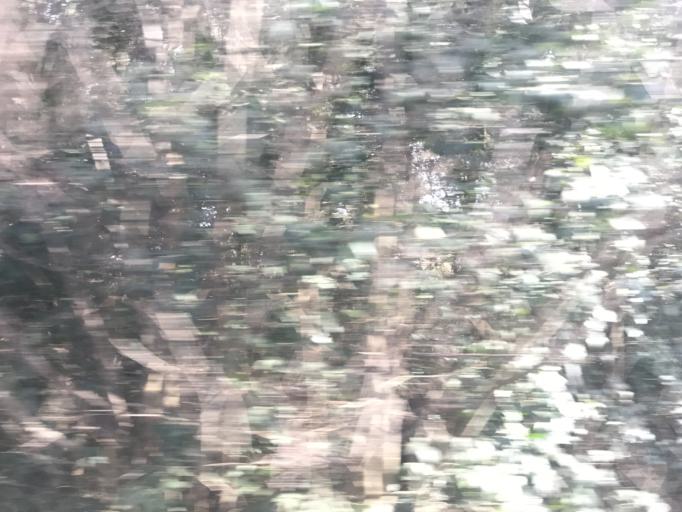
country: AR
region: Cordoba
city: Laguna Larga
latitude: -31.7652
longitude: -63.8133
